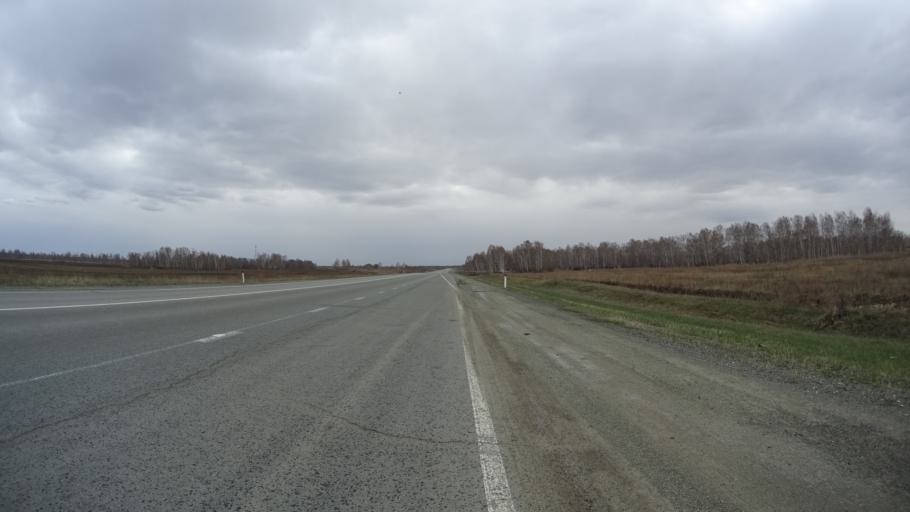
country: RU
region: Chelyabinsk
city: Yemanzhelinsk
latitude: 54.6954
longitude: 61.2497
